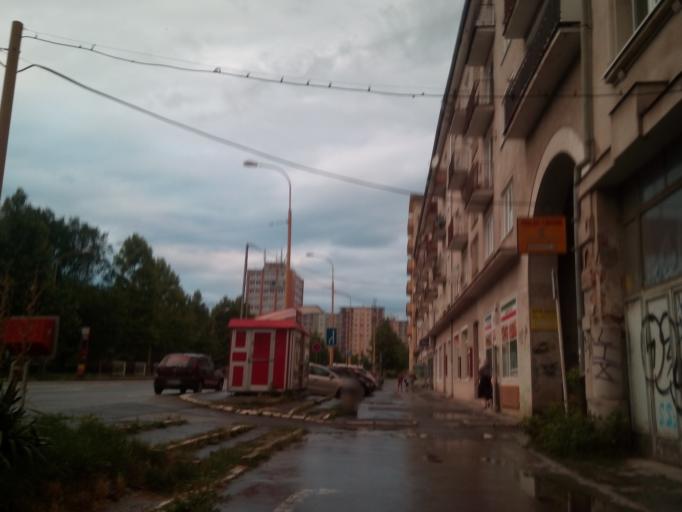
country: SK
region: Kosicky
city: Kosice
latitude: 48.7342
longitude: 21.2481
